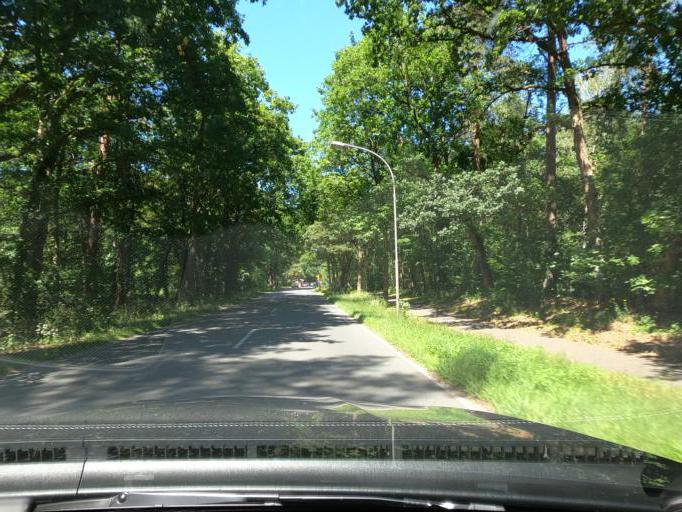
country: DE
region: Lower Saxony
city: Wienhausen
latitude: 52.5723
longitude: 10.1880
